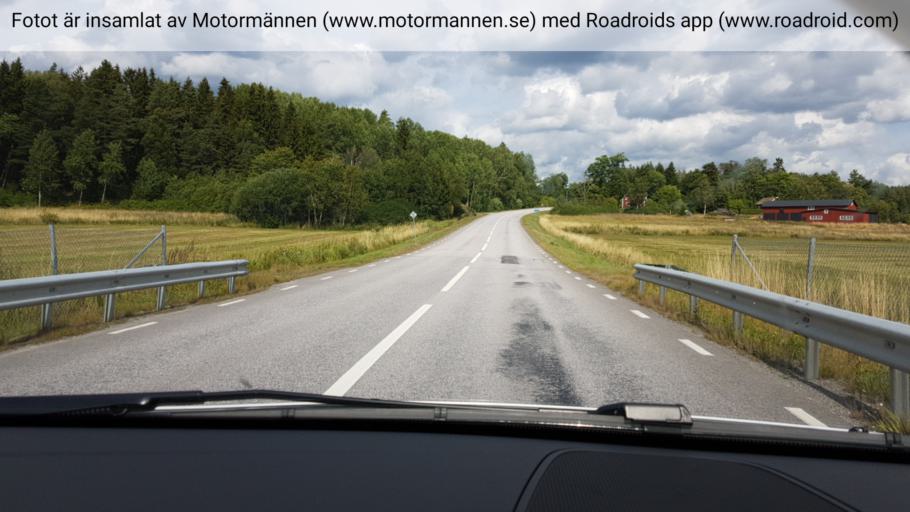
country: SE
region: Stockholm
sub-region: Vallentuna Kommun
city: Vallentuna
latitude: 59.7639
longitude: 18.0421
